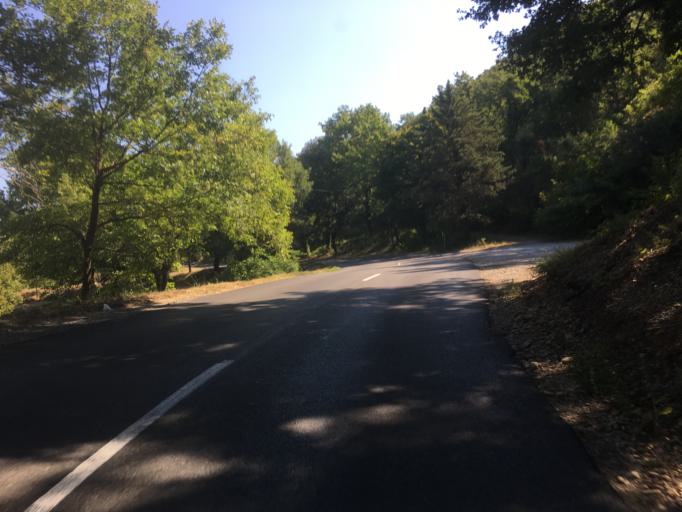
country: FR
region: Provence-Alpes-Cote d'Azur
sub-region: Departement des Alpes-de-Haute-Provence
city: Villeneuve
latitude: 43.8547
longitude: 5.8857
